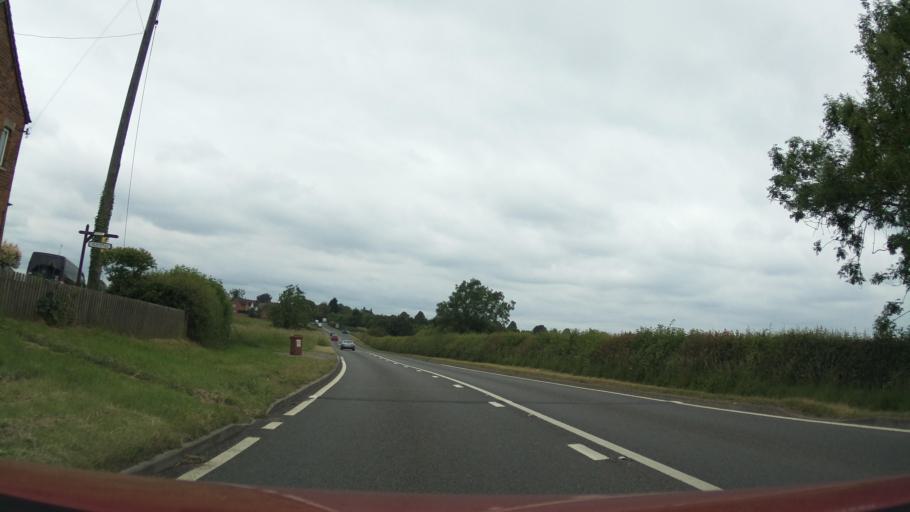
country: GB
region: England
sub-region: Leicestershire
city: Melton Mowbray
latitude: 52.7468
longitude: -0.8669
